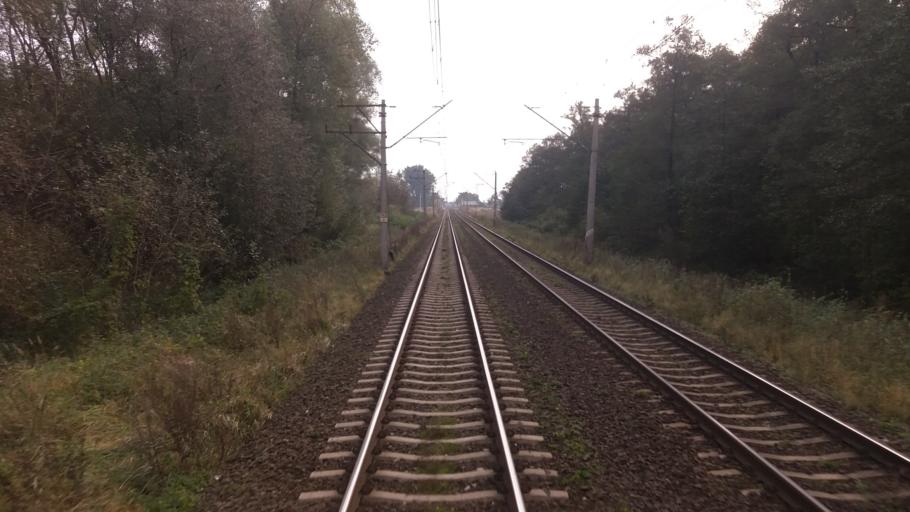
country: PL
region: West Pomeranian Voivodeship
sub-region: Powiat stargardzki
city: Dolice
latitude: 53.2233
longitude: 15.1484
